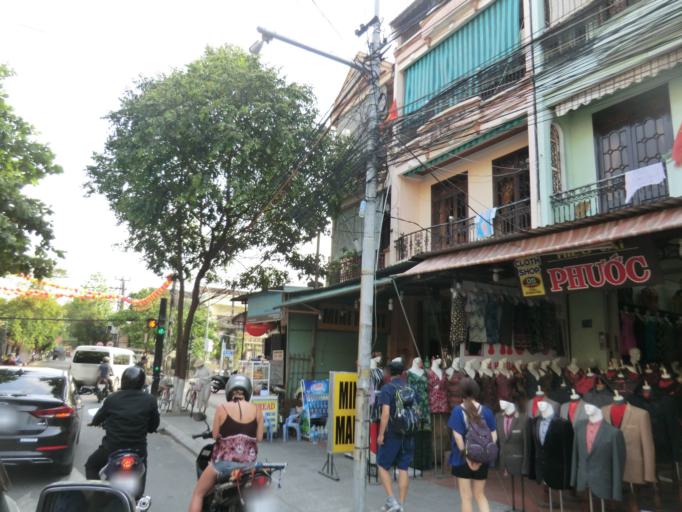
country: VN
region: Quang Nam
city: Hoi An
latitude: 15.8802
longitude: 108.3267
